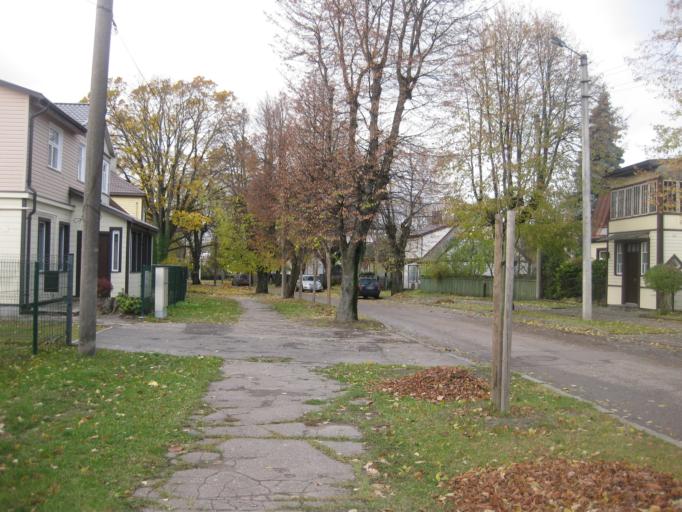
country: LT
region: Kauno apskritis
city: Dainava (Kaunas)
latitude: 54.9039
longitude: 23.9419
